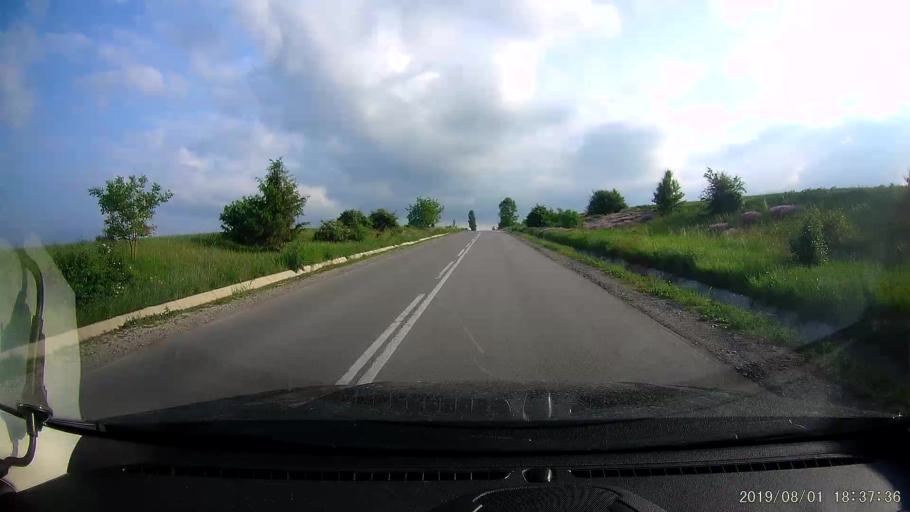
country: BG
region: Shumen
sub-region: Obshtina Khitrino
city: Gara Khitrino
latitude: 43.4177
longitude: 26.9282
